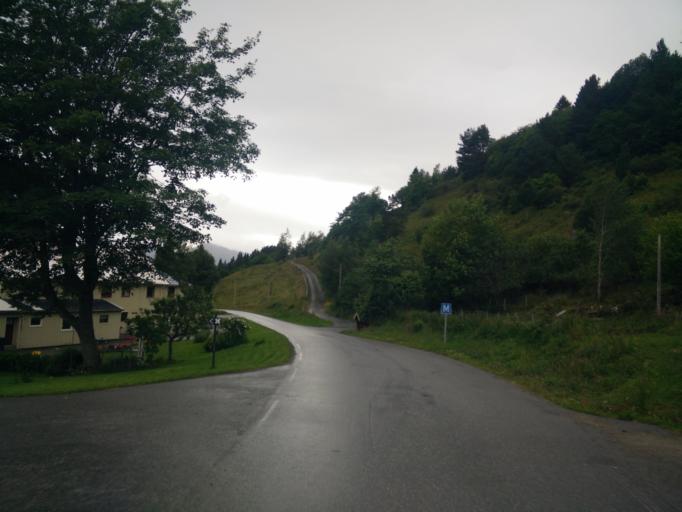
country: NO
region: More og Romsdal
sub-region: Kristiansund
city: Rensvik
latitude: 63.0158
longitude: 7.9100
